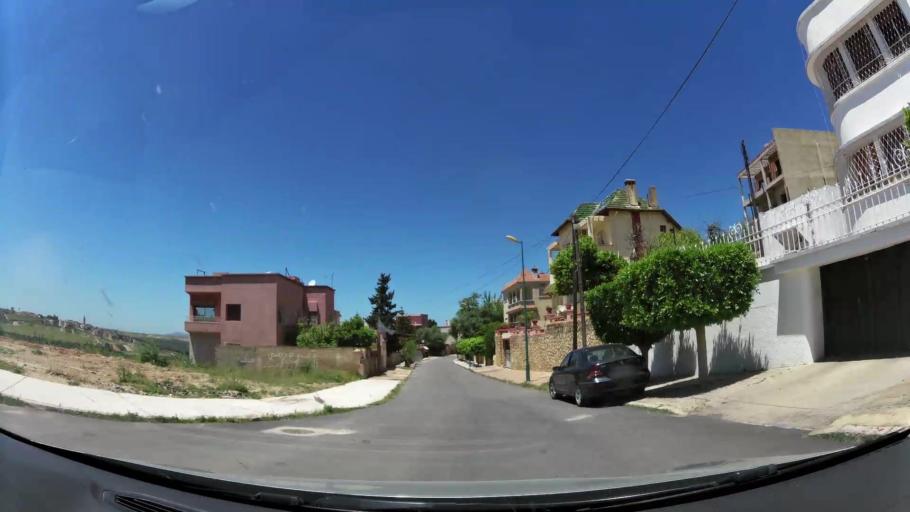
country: MA
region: Meknes-Tafilalet
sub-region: Meknes
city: Meknes
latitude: 33.9095
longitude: -5.5624
